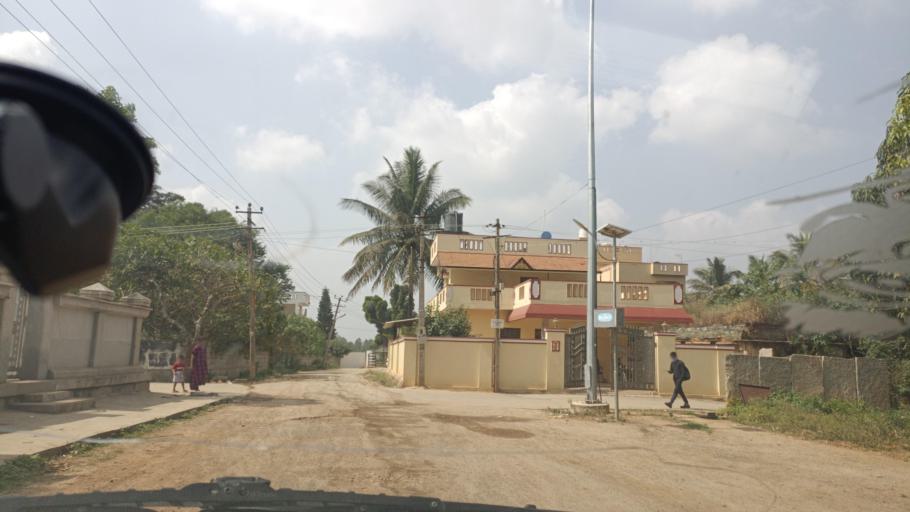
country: IN
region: Karnataka
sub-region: Bangalore Urban
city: Yelahanka
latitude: 13.1683
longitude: 77.6285
